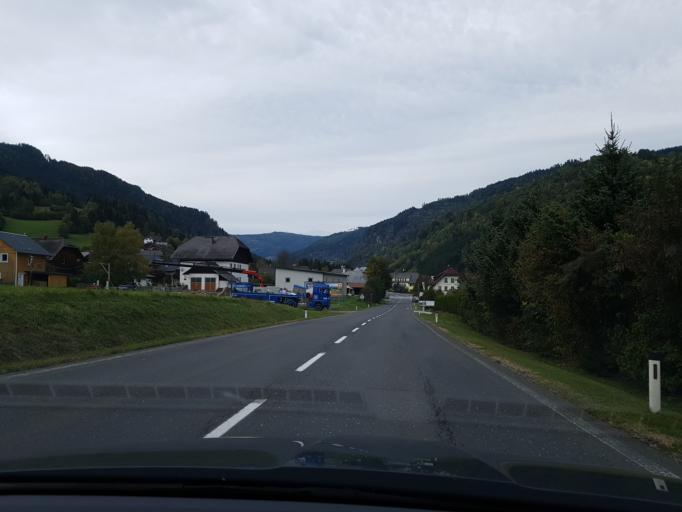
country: AT
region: Salzburg
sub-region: Politischer Bezirk Tamsweg
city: Ramingstein
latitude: 47.0673
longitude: 13.8857
